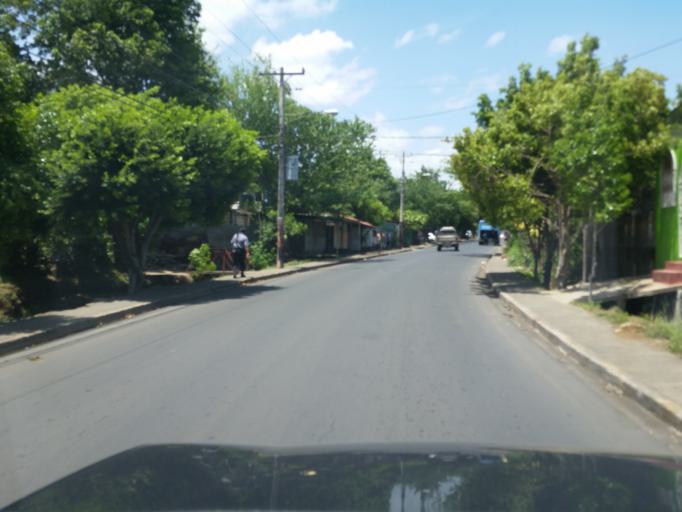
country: NI
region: Managua
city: Managua
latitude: 12.1249
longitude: -86.2086
